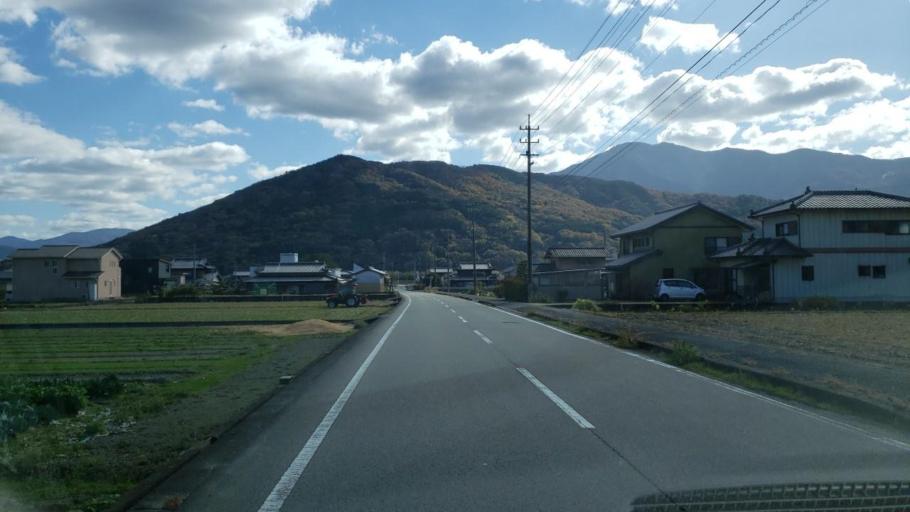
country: JP
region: Tokushima
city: Wakimachi
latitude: 34.0702
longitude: 134.1800
